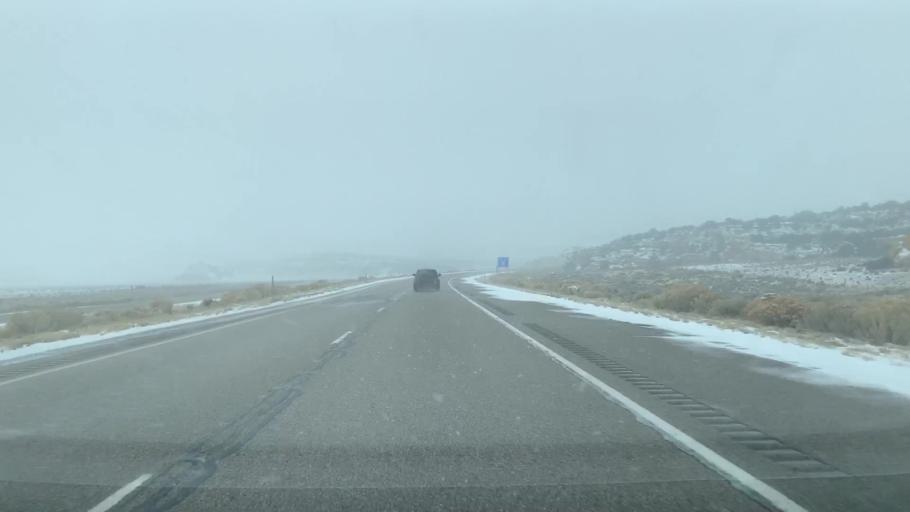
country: US
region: Utah
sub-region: Emery County
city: Ferron
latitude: 38.8658
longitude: -110.7898
